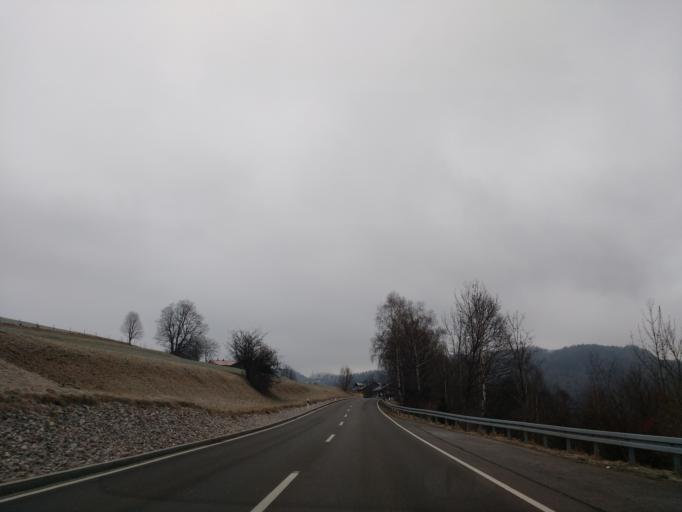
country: AT
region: Tyrol
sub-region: Politischer Bezirk Reutte
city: Vils
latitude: 47.5779
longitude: 10.6307
